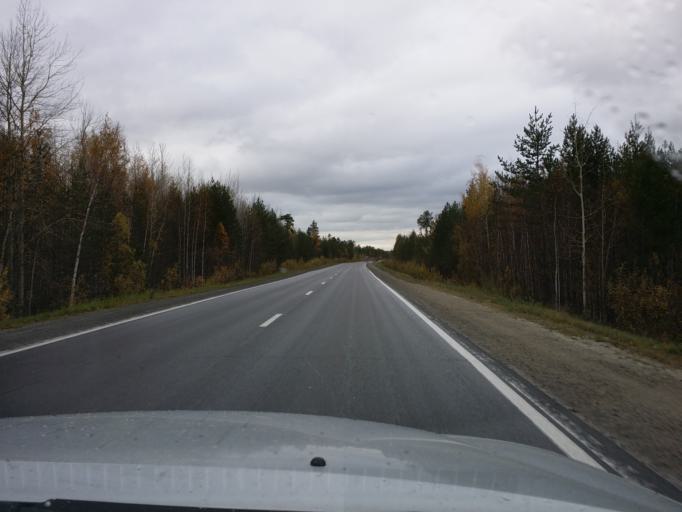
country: RU
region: Khanty-Mansiyskiy Avtonomnyy Okrug
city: Megion
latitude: 61.1091
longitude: 75.8471
